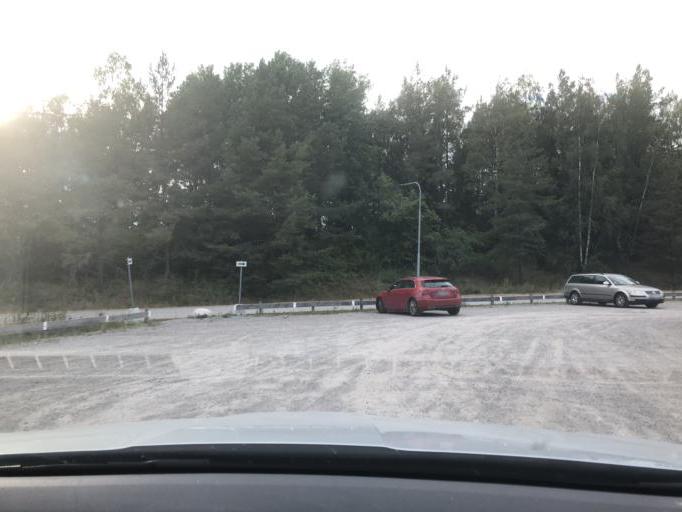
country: SE
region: Stockholm
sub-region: Botkyrka Kommun
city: Tullinge
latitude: 59.2181
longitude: 17.9295
